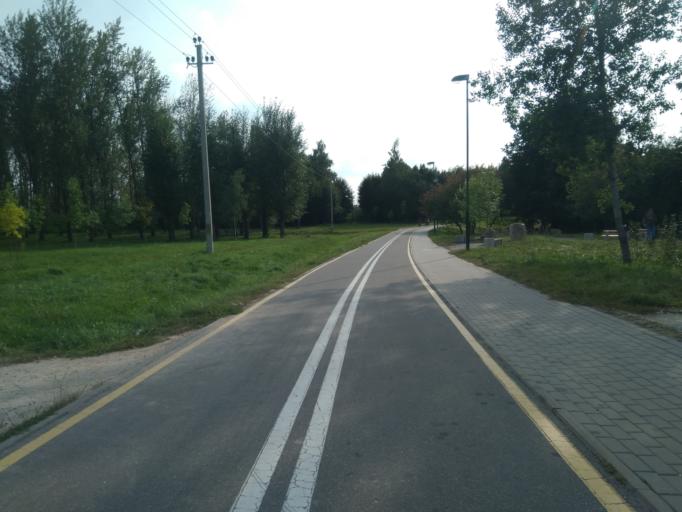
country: BY
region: Minsk
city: Minsk
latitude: 53.8522
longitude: 27.5933
